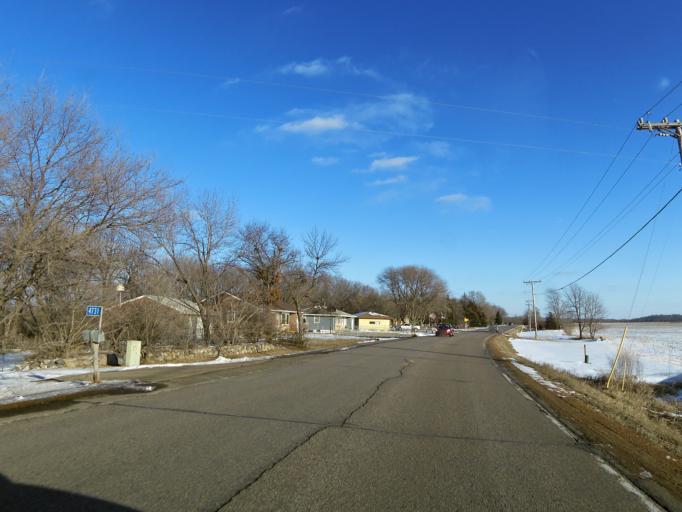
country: US
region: Minnesota
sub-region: Scott County
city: Shakopee
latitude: 44.7746
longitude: -93.4597
